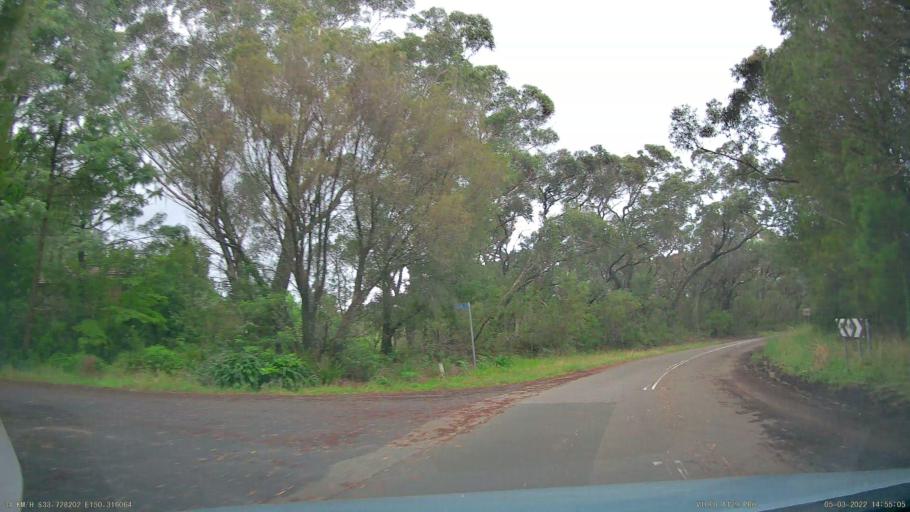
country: AU
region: New South Wales
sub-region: Blue Mountains Municipality
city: Katoomba
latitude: -33.7280
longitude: 150.3161
